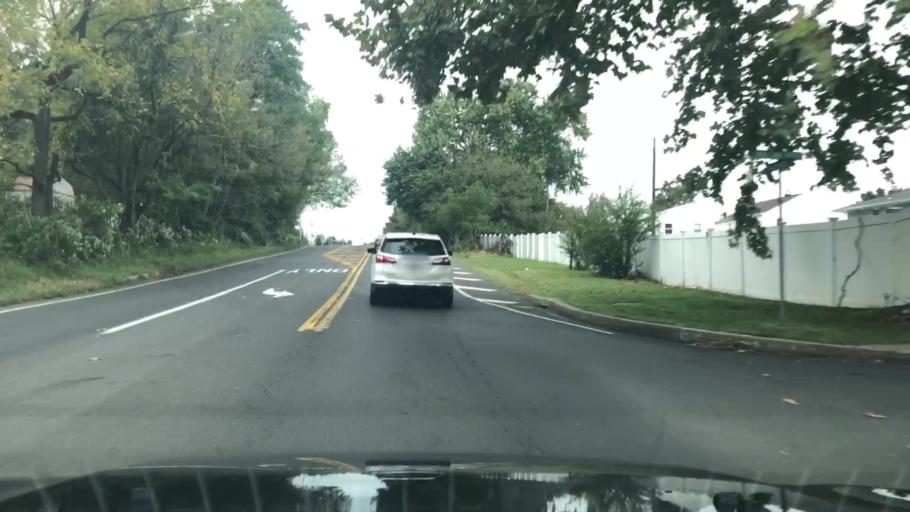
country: US
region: Pennsylvania
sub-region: Bucks County
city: Woodbourne
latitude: 40.1707
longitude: -74.8799
